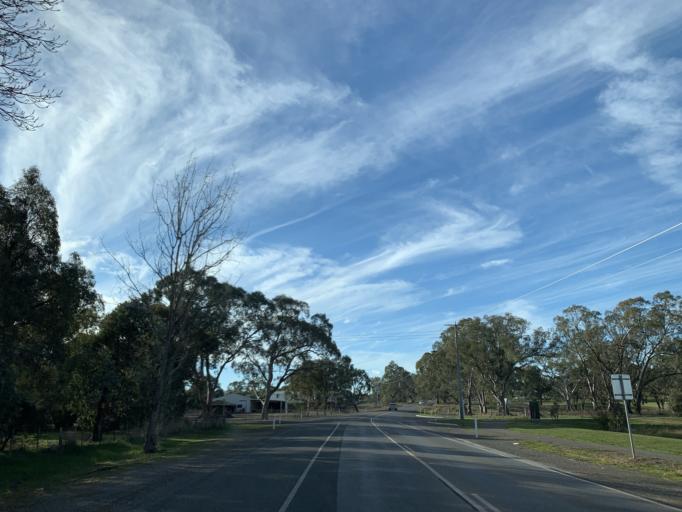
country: AU
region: Victoria
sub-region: Mansfield
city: Mansfield
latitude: -37.0453
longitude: 146.0988
